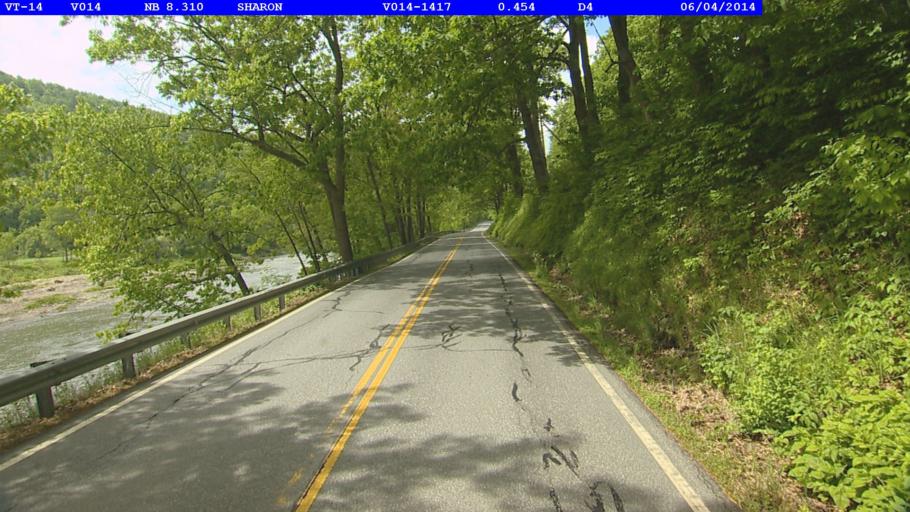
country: US
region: Vermont
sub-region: Windsor County
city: Woodstock
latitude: 43.7264
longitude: -72.4330
